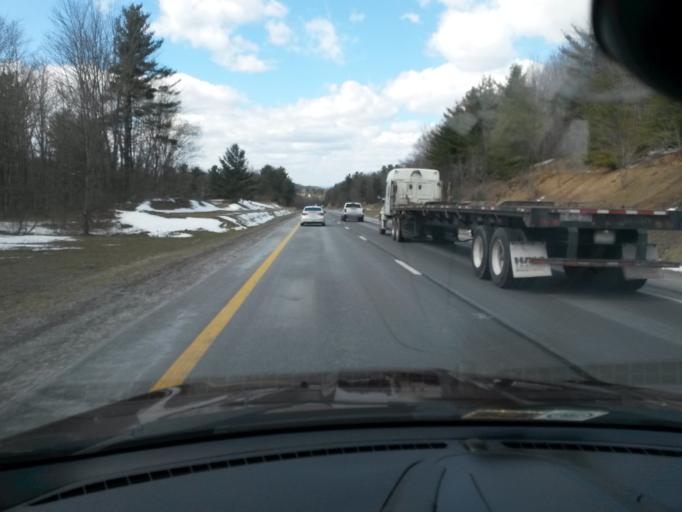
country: US
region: West Virginia
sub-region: Raleigh County
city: Shady Spring
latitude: 37.6553
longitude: -81.1097
